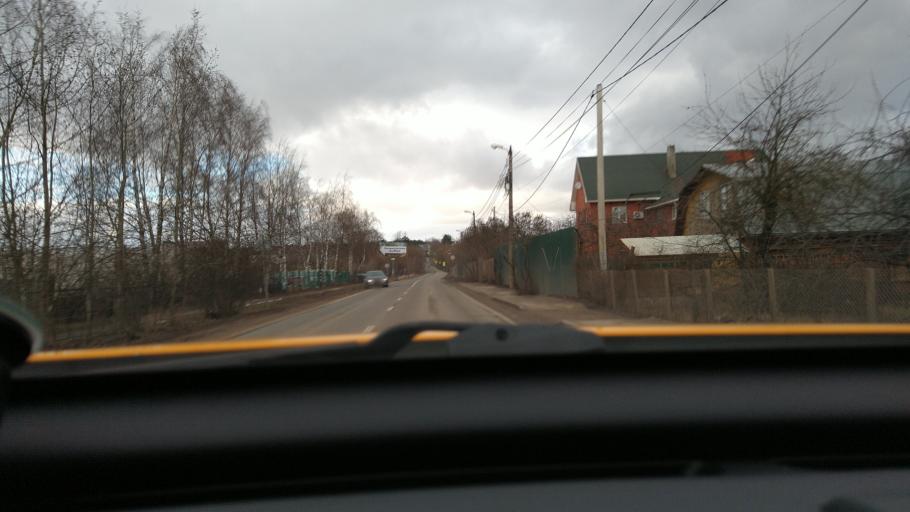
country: RU
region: Moskovskaya
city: Barvikha
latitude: 55.7614
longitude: 37.2297
